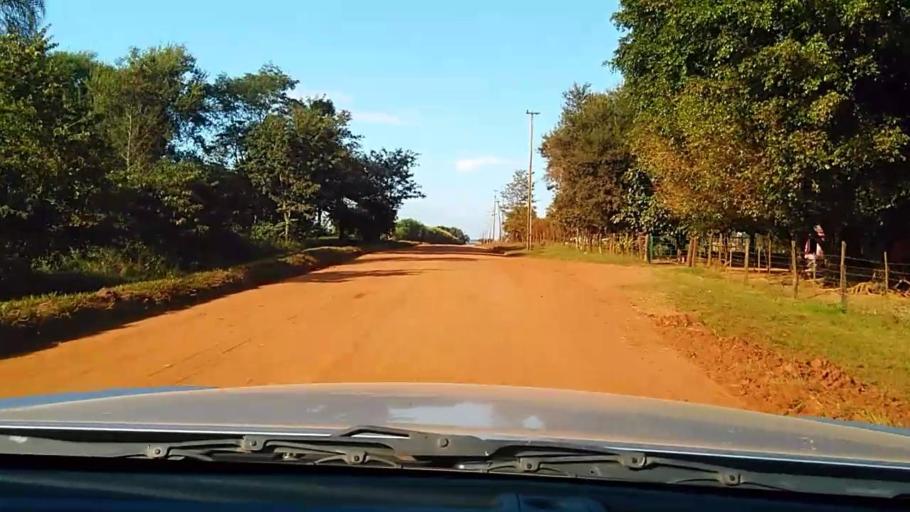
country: PY
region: Alto Parana
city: Doctor Juan Leon Mallorquin
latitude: -25.6927
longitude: -55.3782
